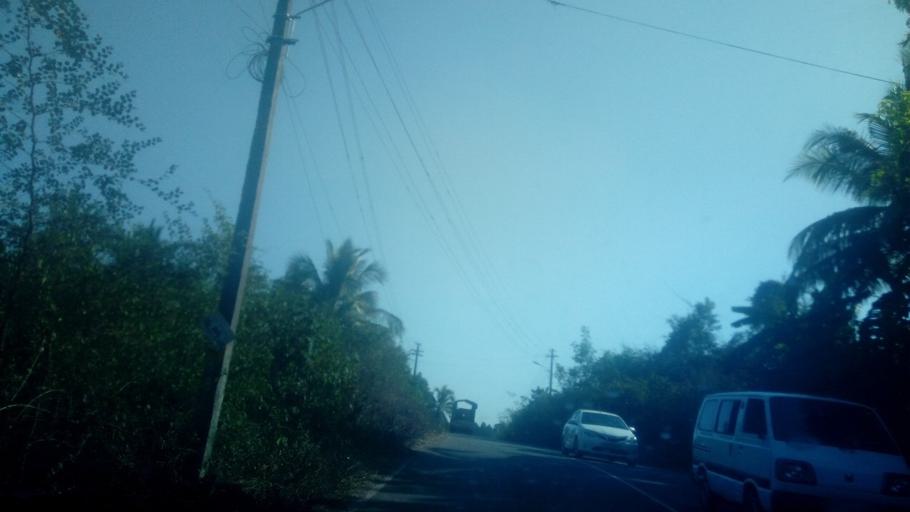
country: IN
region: Goa
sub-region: North Goa
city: Sanquelim
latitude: 15.5393
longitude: 74.0104
